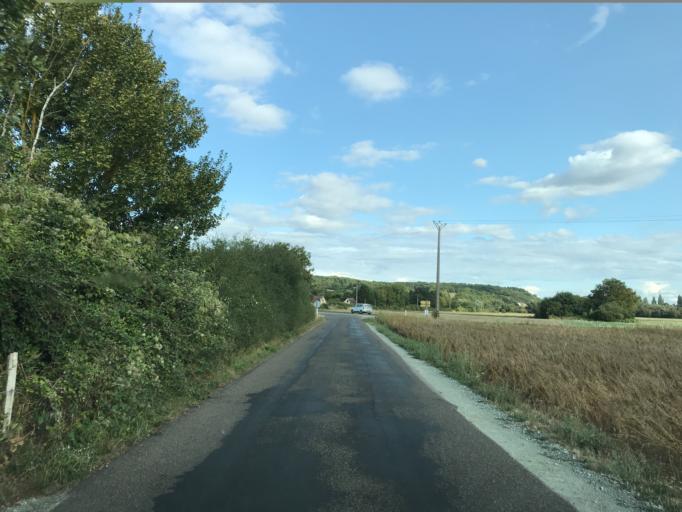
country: FR
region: Haute-Normandie
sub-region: Departement de l'Eure
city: Houlbec-Cocherel
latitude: 49.0560
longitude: 1.3270
